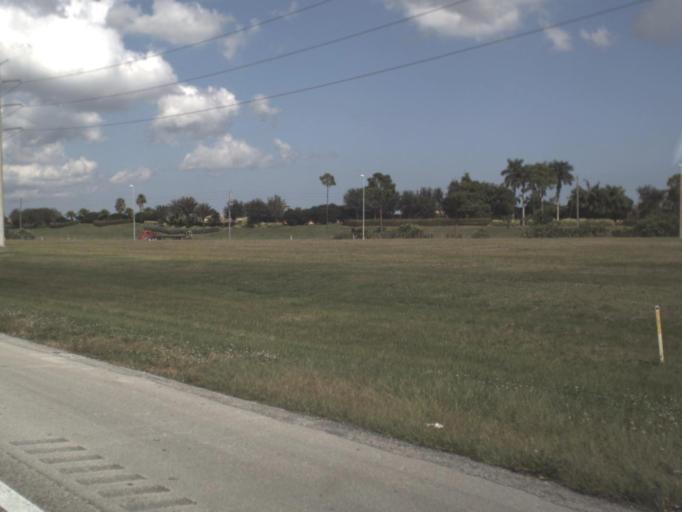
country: US
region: Florida
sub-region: Martin County
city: North River Shores
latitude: 27.2123
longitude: -80.3349
